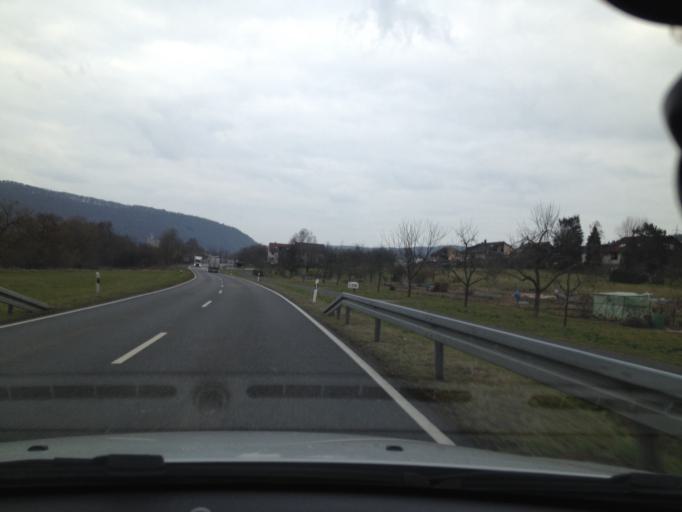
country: DE
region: Bavaria
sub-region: Regierungsbezirk Unterfranken
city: Faulbach
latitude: 49.7734
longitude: 9.4706
